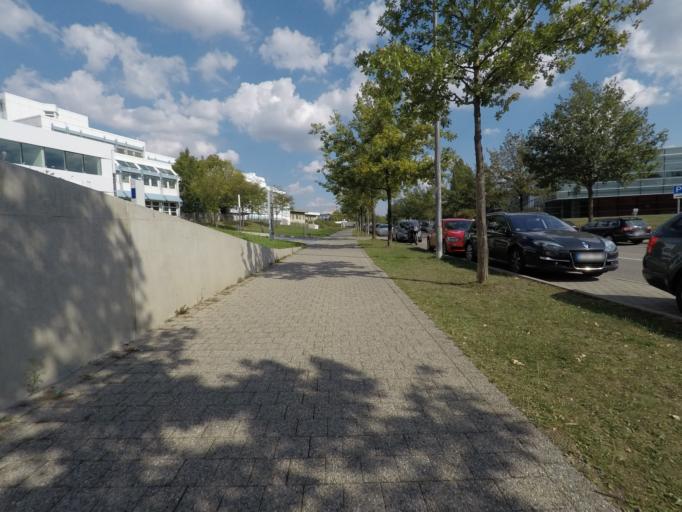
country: DE
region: Baden-Wuerttemberg
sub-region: Regierungsbezirk Stuttgart
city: Gerlingen
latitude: 48.7399
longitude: 9.0962
